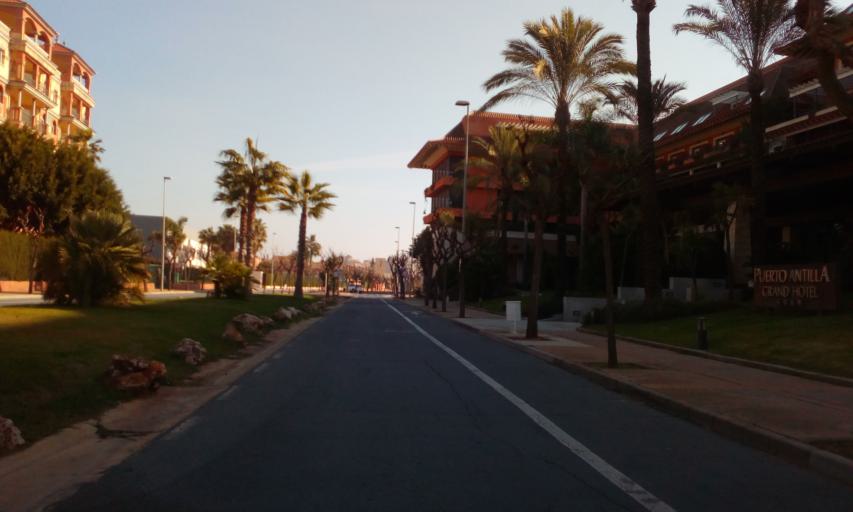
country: ES
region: Andalusia
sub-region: Provincia de Huelva
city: Lepe
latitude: 37.2070
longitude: -7.2310
